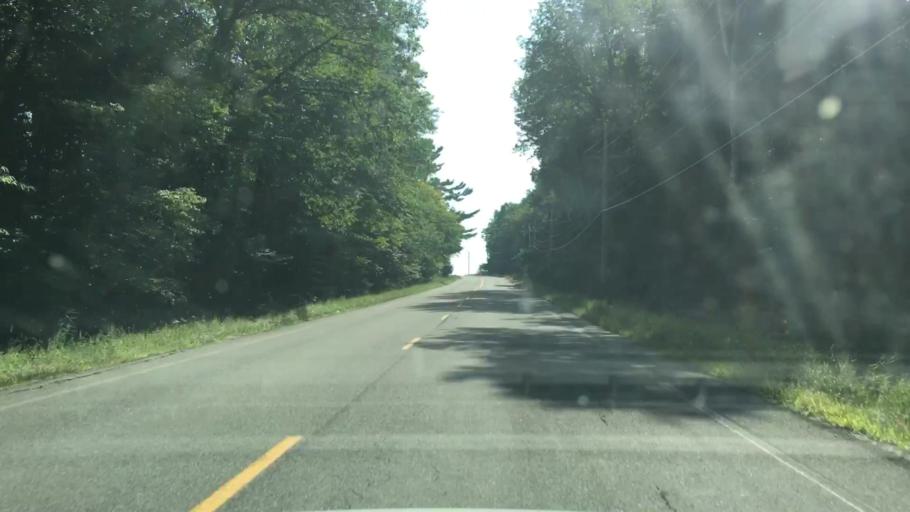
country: US
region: Maine
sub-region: Penobscot County
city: Lincoln
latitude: 45.4030
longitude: -68.5064
